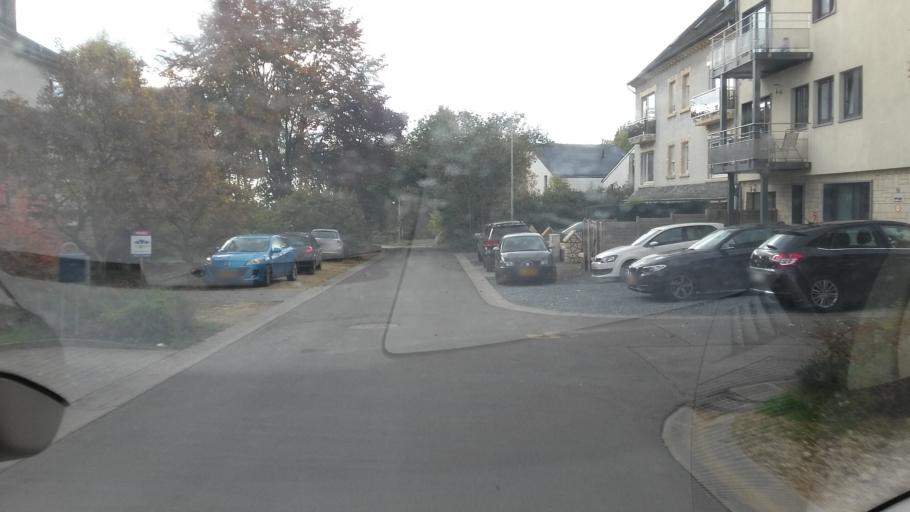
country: BE
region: Wallonia
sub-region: Province du Luxembourg
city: Arlon
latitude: 49.6844
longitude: 5.8261
